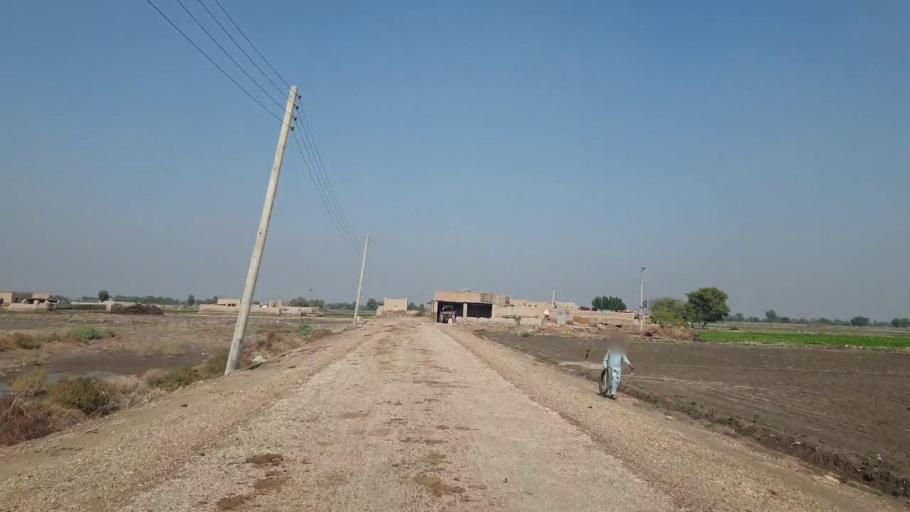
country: PK
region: Sindh
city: Sehwan
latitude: 26.4239
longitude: 67.8103
